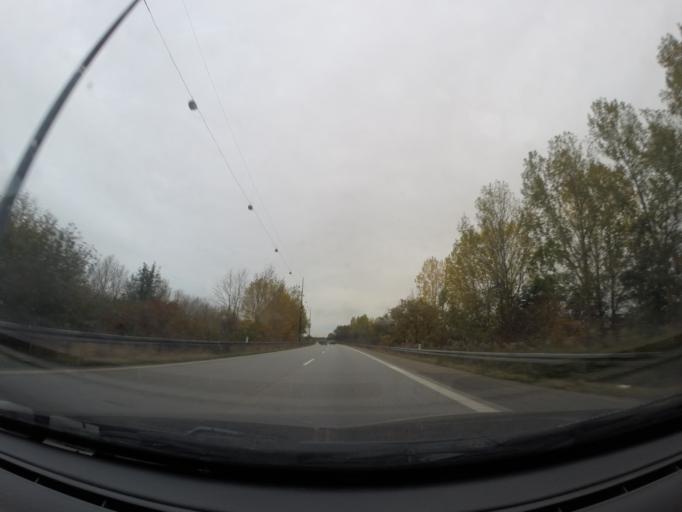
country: DK
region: Capital Region
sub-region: Ishoj Kommune
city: Ishoj
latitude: 55.6394
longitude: 12.3365
